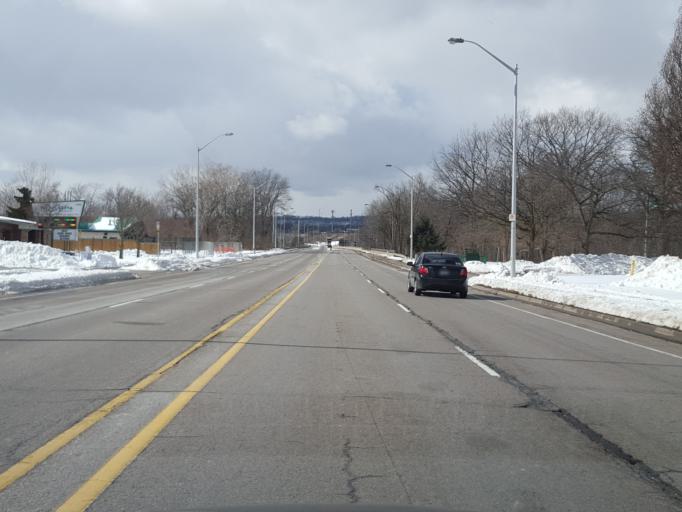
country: CA
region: Ontario
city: Hamilton
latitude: 43.2912
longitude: -79.8791
